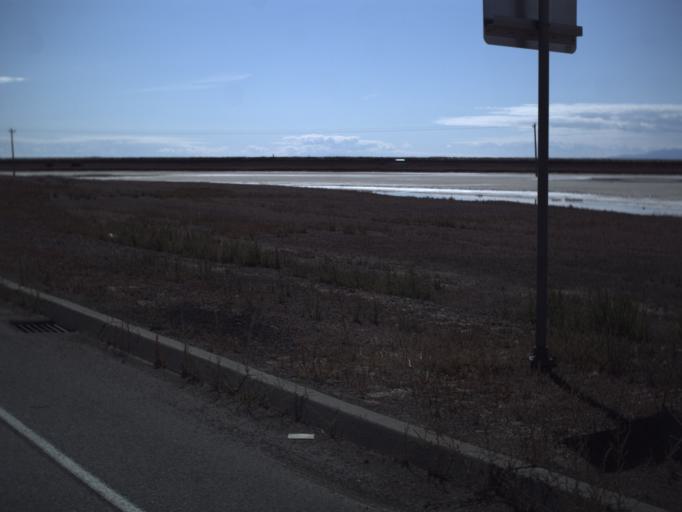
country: US
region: Utah
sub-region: Tooele County
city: Wendover
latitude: 40.7381
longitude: -113.8584
